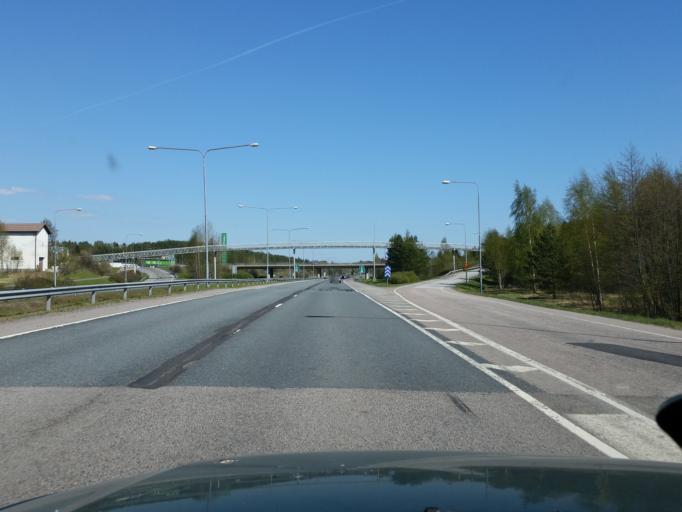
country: FI
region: Uusimaa
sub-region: Helsinki
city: Kirkkonummi
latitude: 60.1164
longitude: 24.4376
